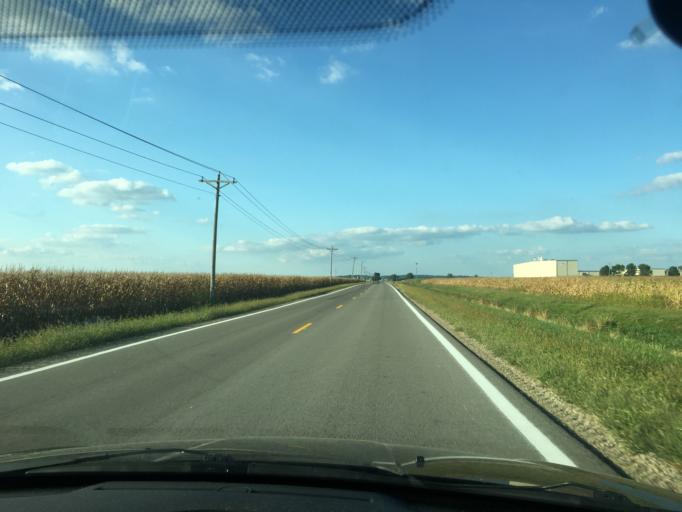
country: US
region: Ohio
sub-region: Logan County
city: West Liberty
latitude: 40.1806
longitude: -83.7825
